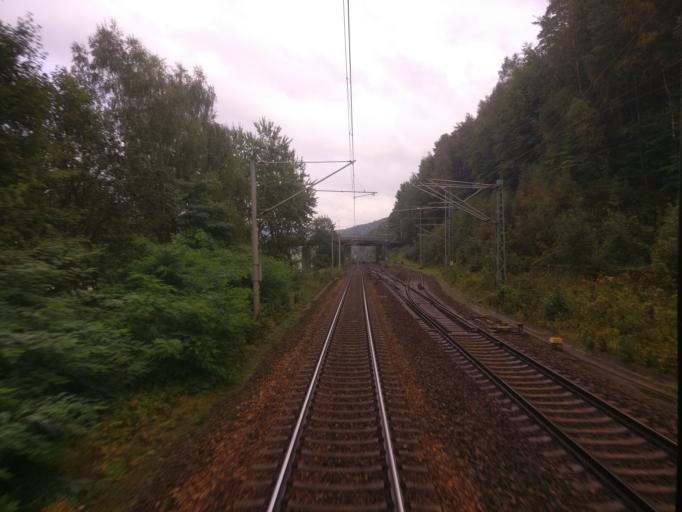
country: DE
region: Saxony
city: Bad Schandau
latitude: 50.9168
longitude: 14.1474
